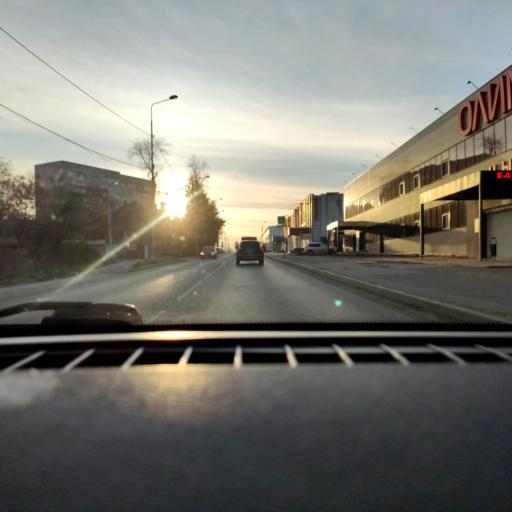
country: RU
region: Perm
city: Kondratovo
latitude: 57.9618
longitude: 56.1619
